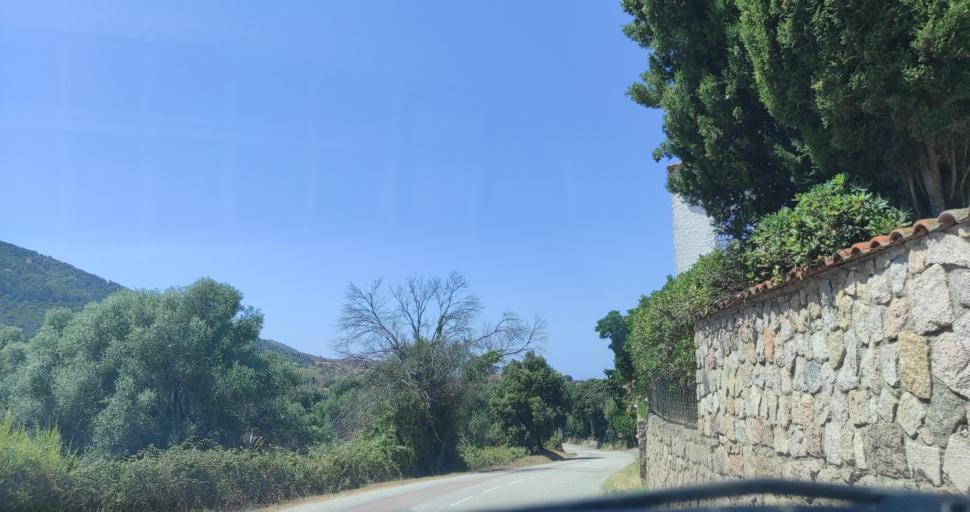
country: FR
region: Corsica
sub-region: Departement de la Corse-du-Sud
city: Alata
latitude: 41.9625
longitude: 8.7250
